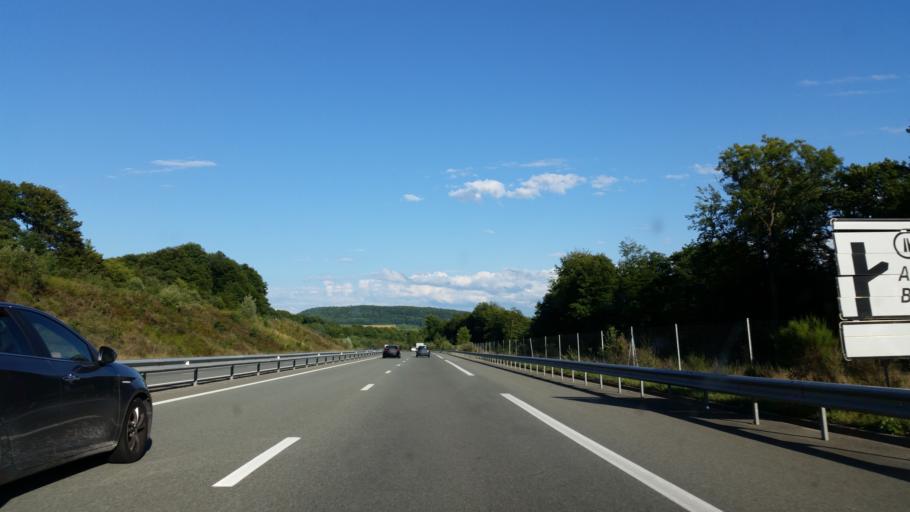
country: FR
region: Franche-Comte
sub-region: Departement de la Haute-Saone
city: Hericourt
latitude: 47.6071
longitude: 6.7043
